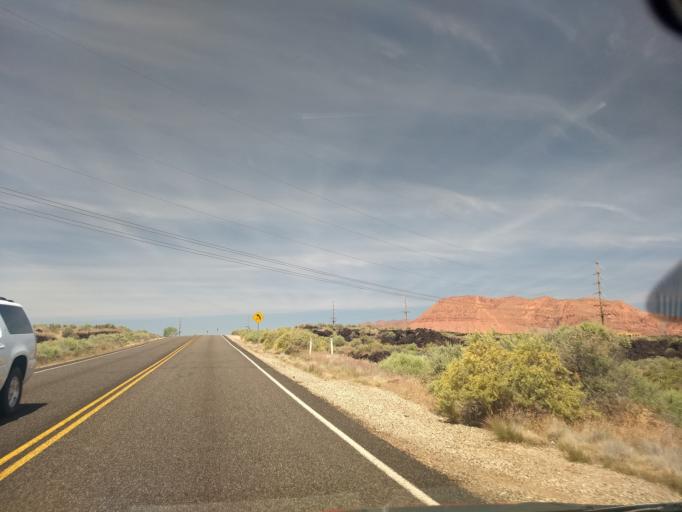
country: US
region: Utah
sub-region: Washington County
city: Santa Clara
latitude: 37.1431
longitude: -113.6451
